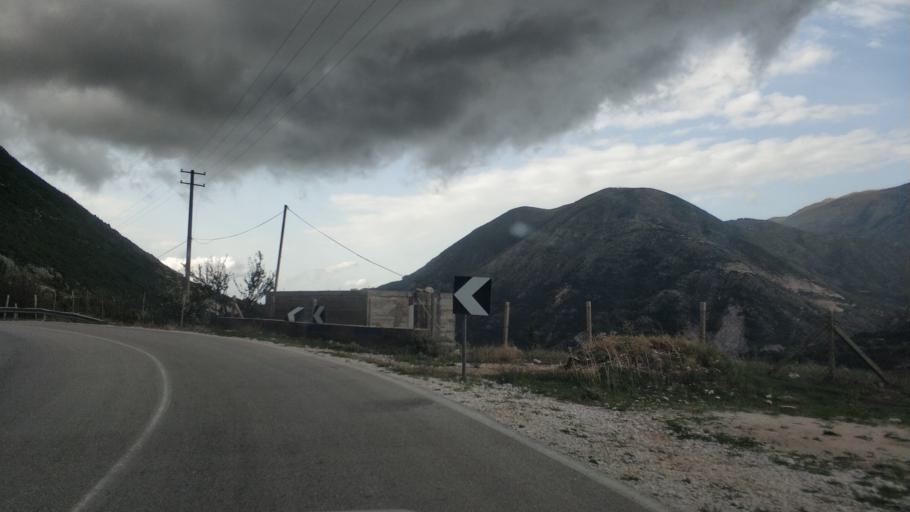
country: AL
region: Vlore
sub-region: Rrethi i Vlores
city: Brataj
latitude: 40.2364
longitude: 19.5550
